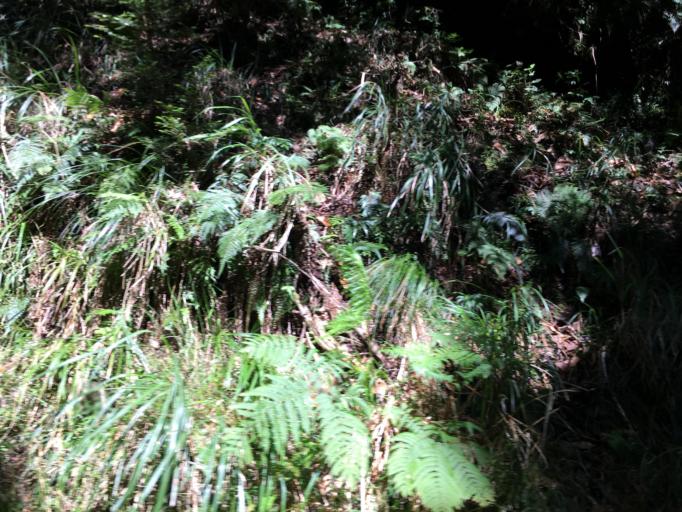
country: TW
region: Taiwan
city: Daxi
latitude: 24.5672
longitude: 121.4141
